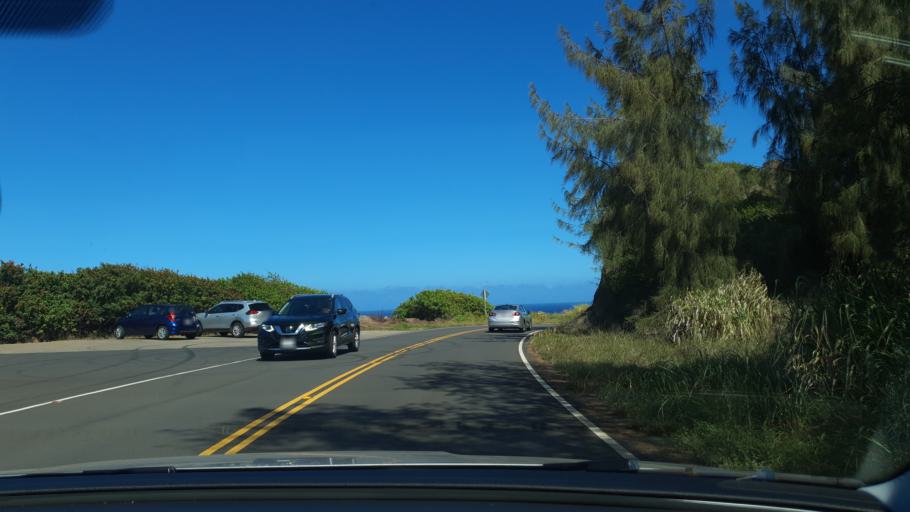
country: US
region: Hawaii
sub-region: Maui County
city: Napili-Honokowai
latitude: 21.0158
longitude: -156.5767
